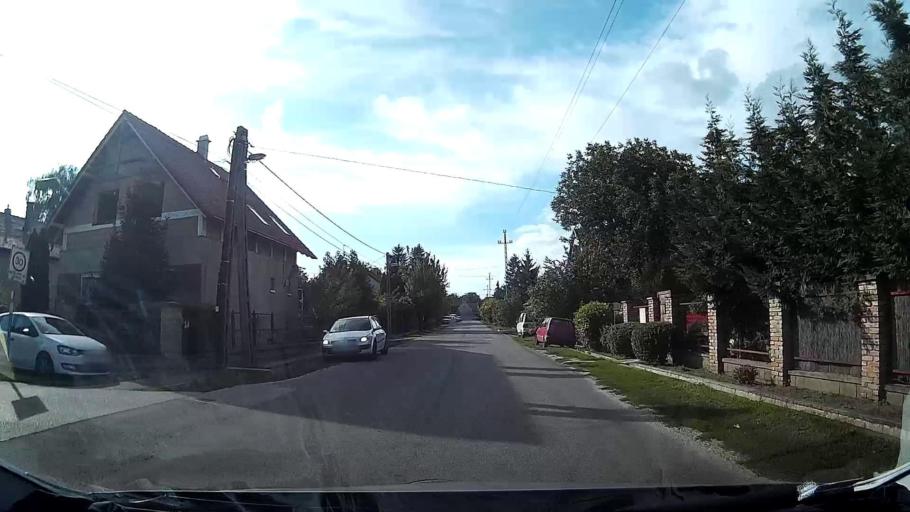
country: HU
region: Pest
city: Pomaz
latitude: 47.6373
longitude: 19.0274
